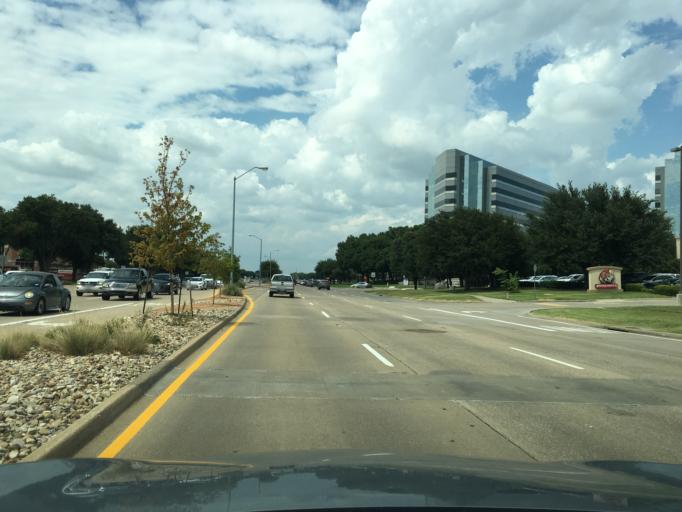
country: US
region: Texas
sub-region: Dallas County
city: Addison
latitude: 33.0219
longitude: -96.7951
